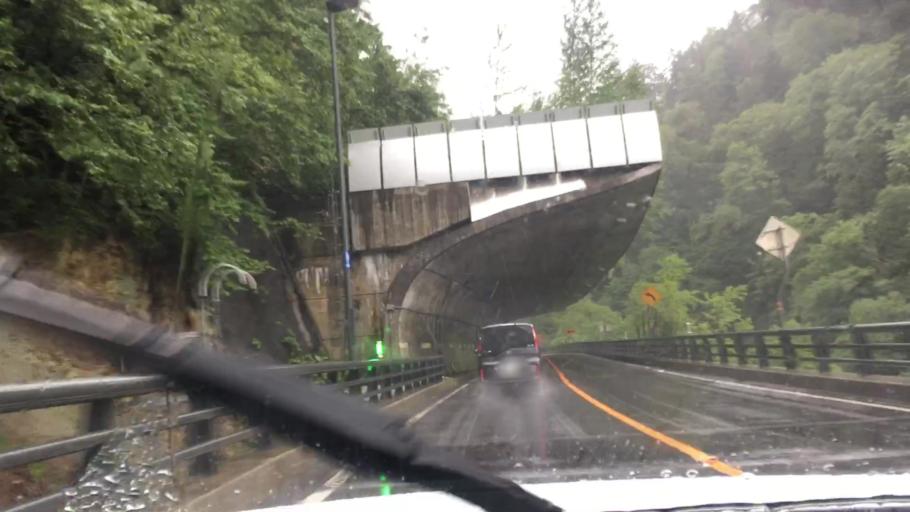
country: JP
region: Hokkaido
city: Sapporo
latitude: 42.9000
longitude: 141.1304
